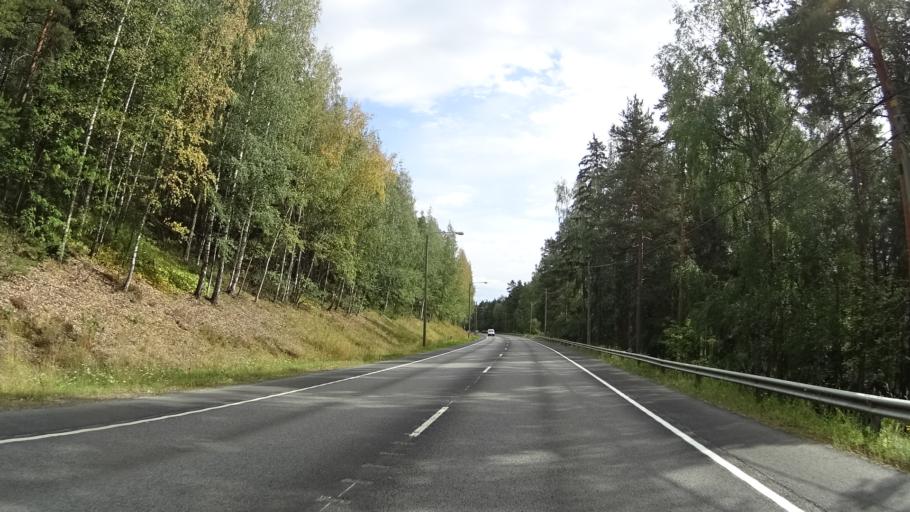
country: FI
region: Pirkanmaa
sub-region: Tampere
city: Kangasala
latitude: 61.4320
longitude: 24.1279
